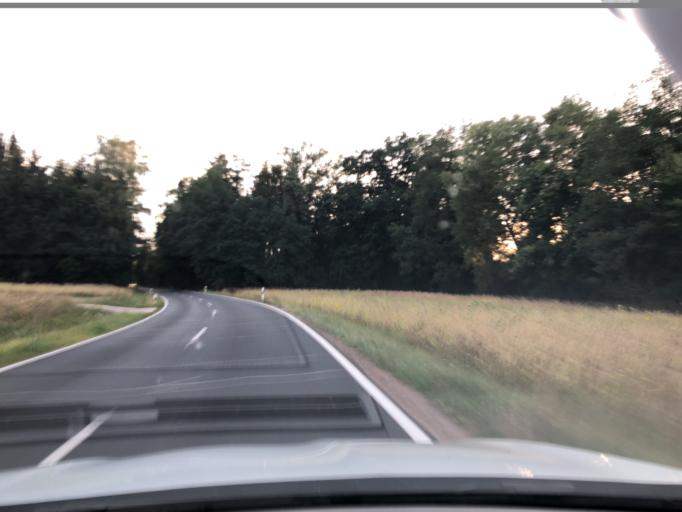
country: DE
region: Bavaria
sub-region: Upper Palatinate
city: Poppenricht
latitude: 49.4908
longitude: 11.8093
